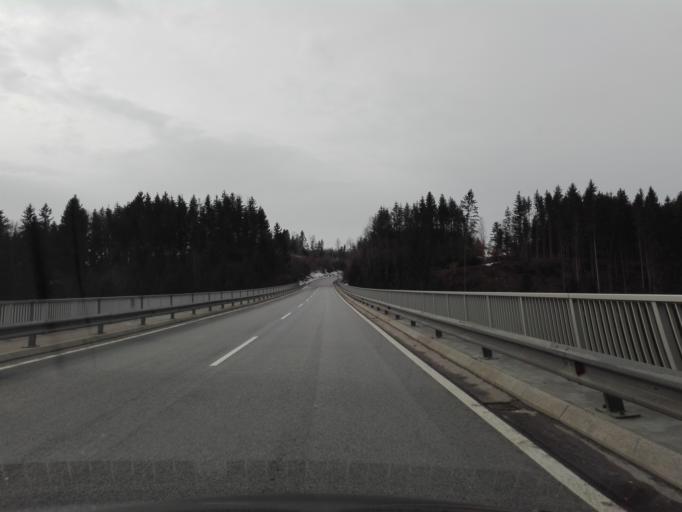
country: AT
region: Upper Austria
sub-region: Politischer Bezirk Rohrbach
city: Atzesberg
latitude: 48.5042
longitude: 13.9399
